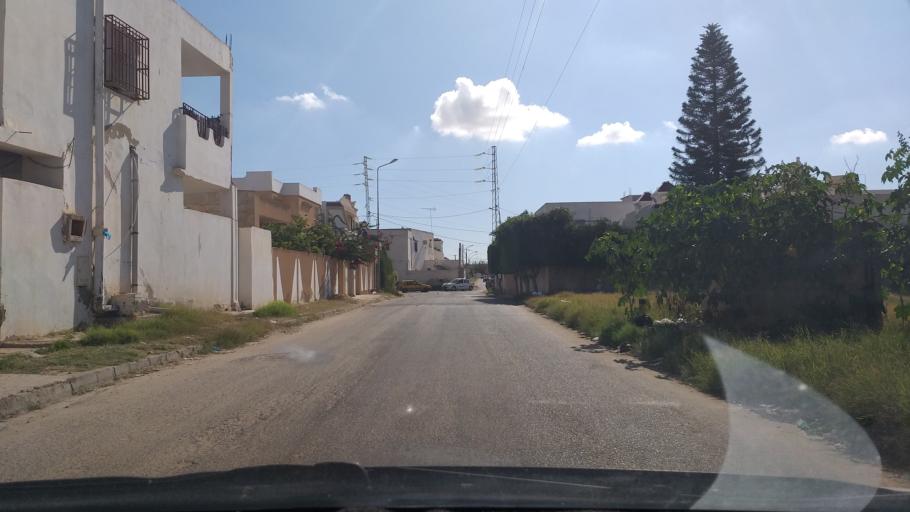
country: TN
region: Safaqis
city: Al Qarmadah
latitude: 34.8006
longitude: 10.7736
